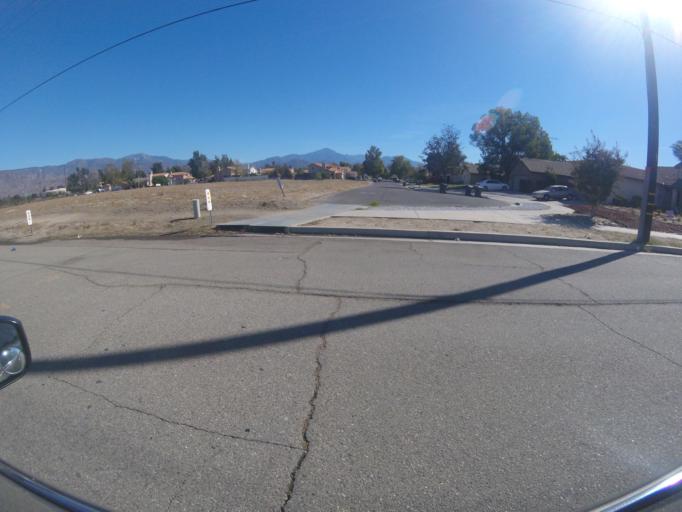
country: US
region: California
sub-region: San Bernardino County
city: Redlands
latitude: 34.0755
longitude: -117.1911
